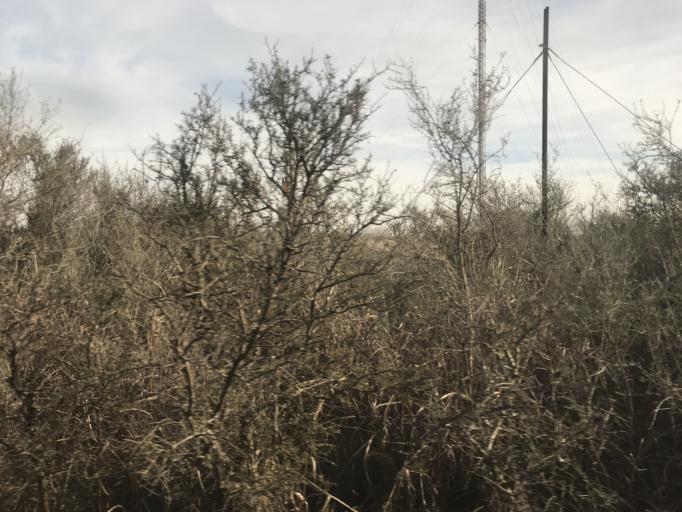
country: AR
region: Cordoba
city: Pilar
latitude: -31.7058
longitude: -63.8651
